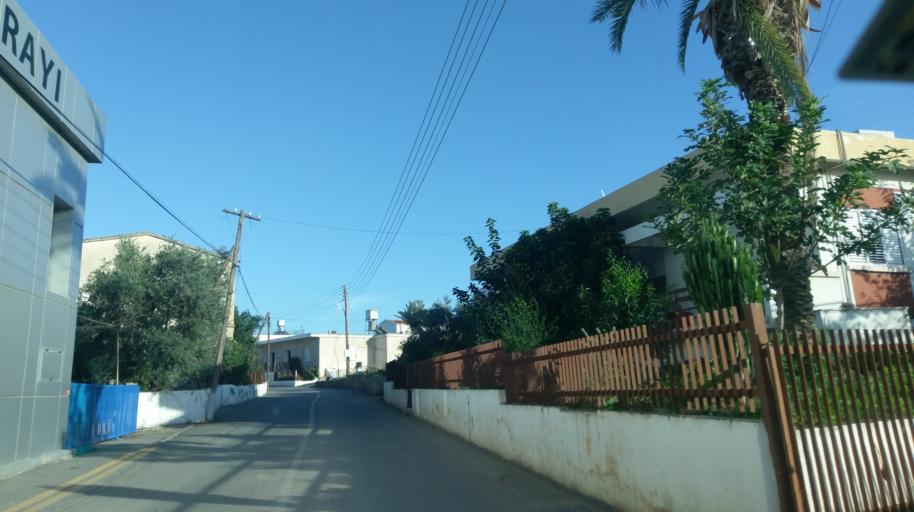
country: CY
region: Ammochostos
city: Lefkonoiko
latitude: 35.3411
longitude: 33.5826
